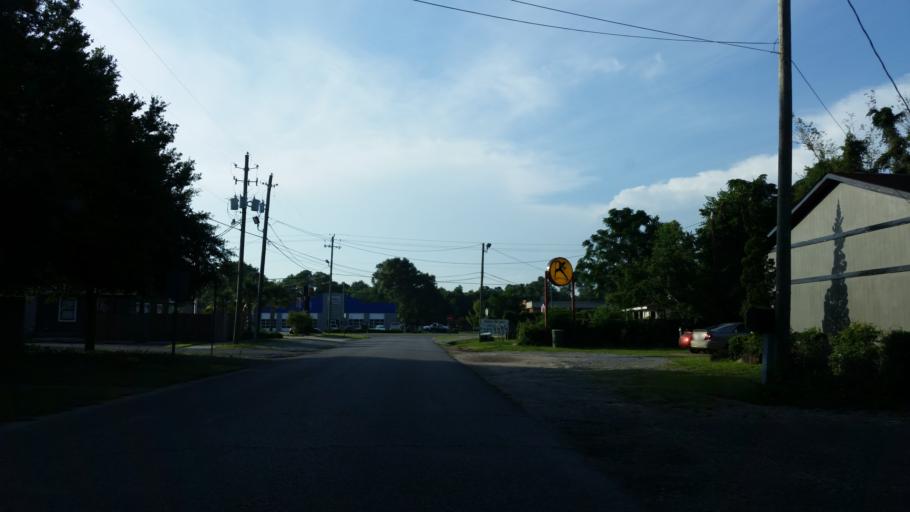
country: US
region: Florida
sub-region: Escambia County
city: Ferry Pass
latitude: 30.4870
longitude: -87.2003
